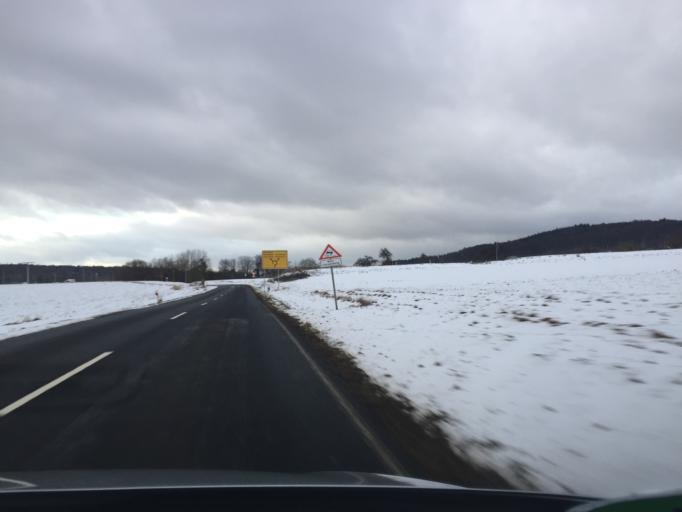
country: DE
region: Bavaria
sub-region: Regierungsbezirk Unterfranken
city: Geiselbach
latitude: 50.1173
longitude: 9.2037
